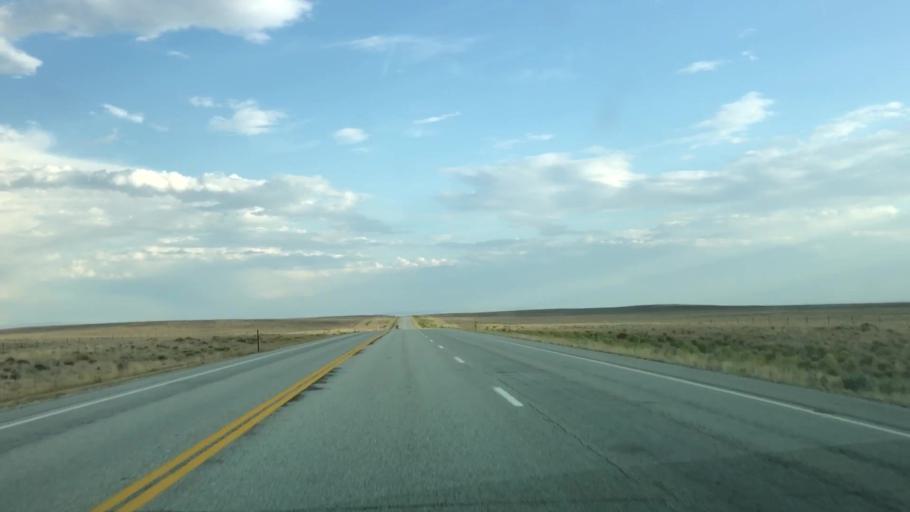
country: US
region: Wyoming
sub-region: Sweetwater County
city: North Rock Springs
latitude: 42.2746
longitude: -109.4818
